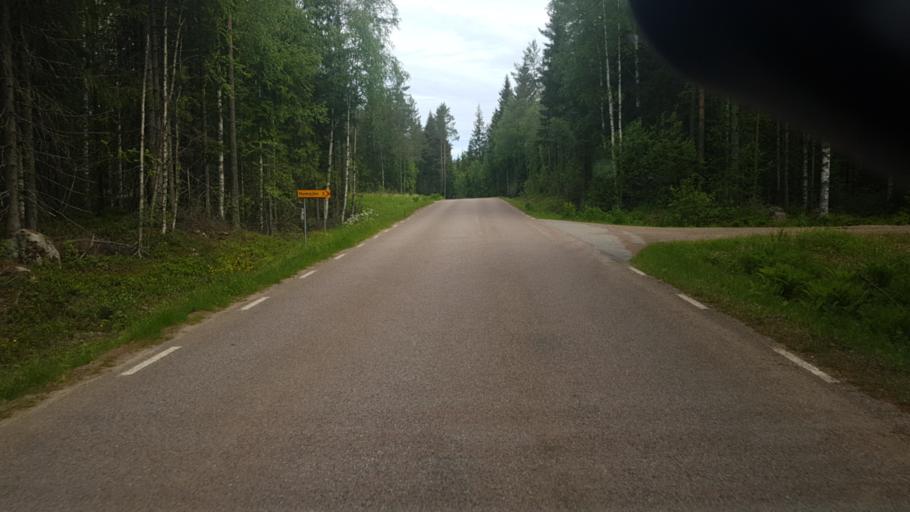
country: SE
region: Vaermland
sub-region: Arvika Kommun
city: Arvika
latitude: 59.7962
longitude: 12.8380
